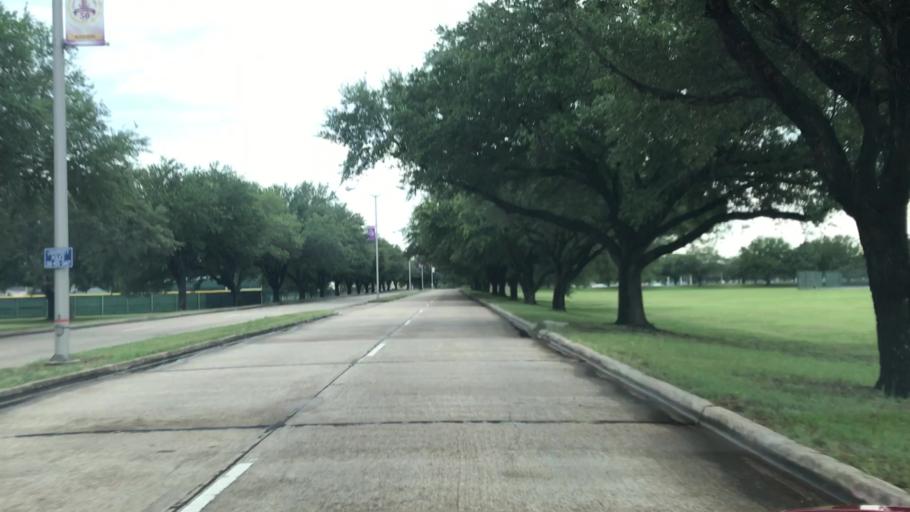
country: US
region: Louisiana
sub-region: Bossier Parish
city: Bossier City
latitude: 32.4283
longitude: -93.6983
